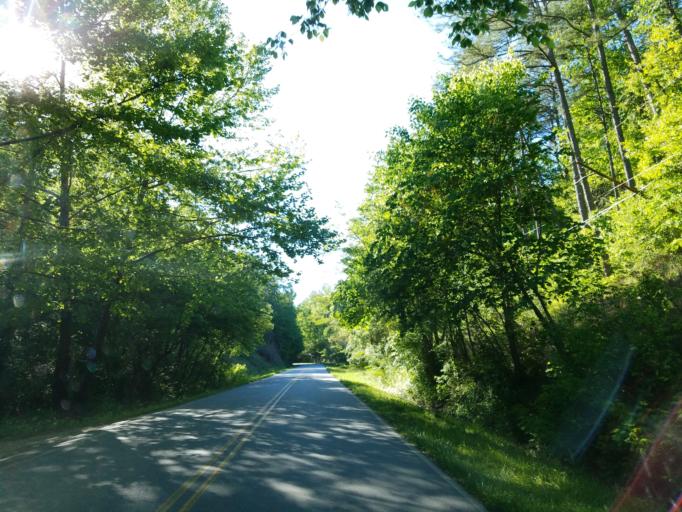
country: US
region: Georgia
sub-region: Pickens County
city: Jasper
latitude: 34.5660
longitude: -84.5131
